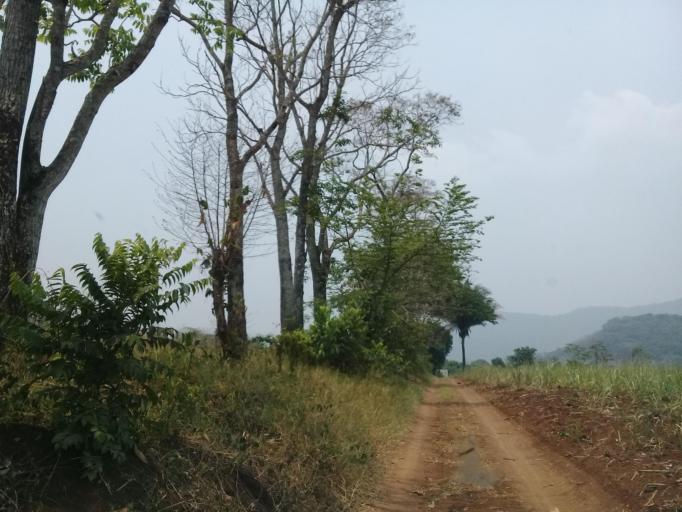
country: MX
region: Veracruz
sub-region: Tezonapa
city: Laguna Chica (Pueblo Nuevo)
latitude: 18.5386
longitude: -96.7382
